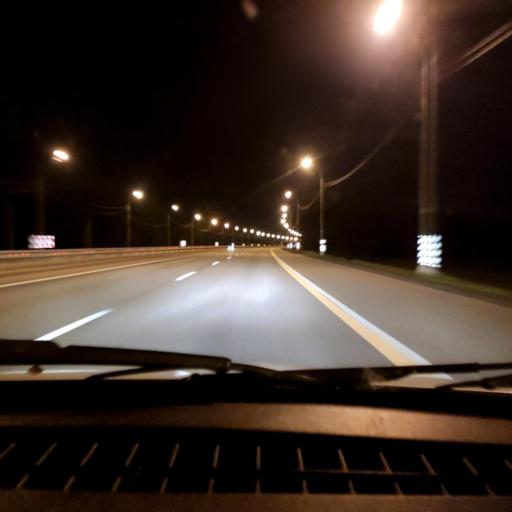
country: RU
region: Lipetsk
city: Zadonsk
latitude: 52.3821
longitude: 38.8753
